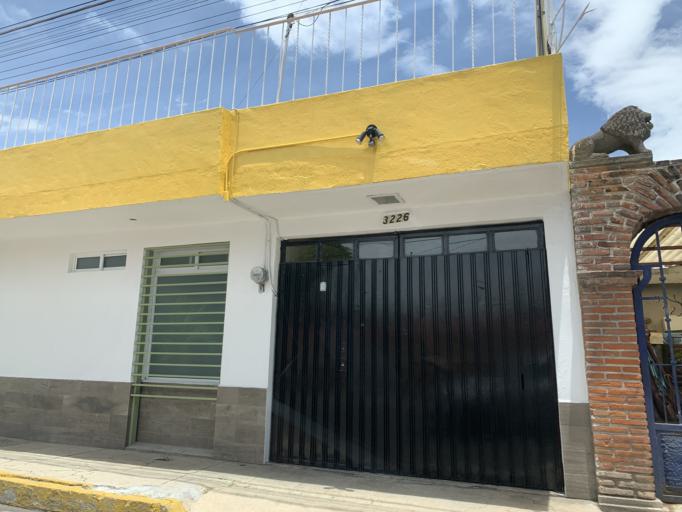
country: MX
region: Puebla
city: Puebla
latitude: 19.0724
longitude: -98.2138
